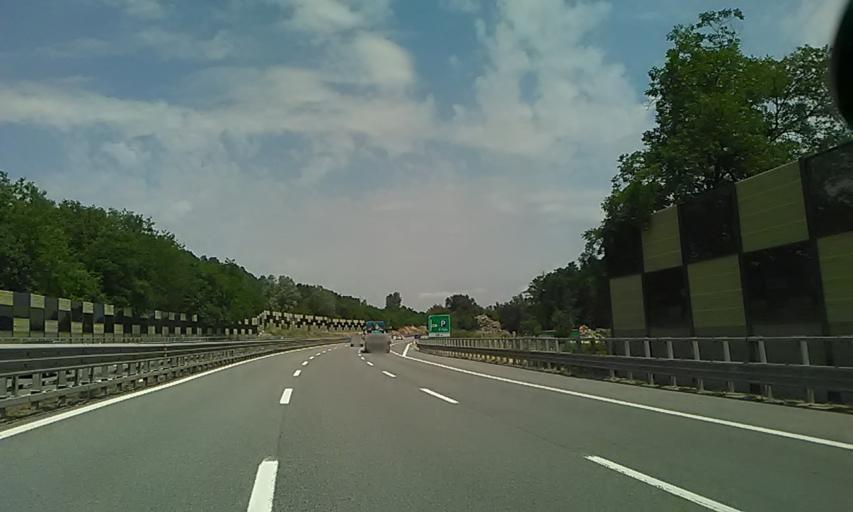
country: IT
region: Piedmont
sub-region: Provincia di Alessandria
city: Rocca Grimalda
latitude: 44.6767
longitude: 8.6583
